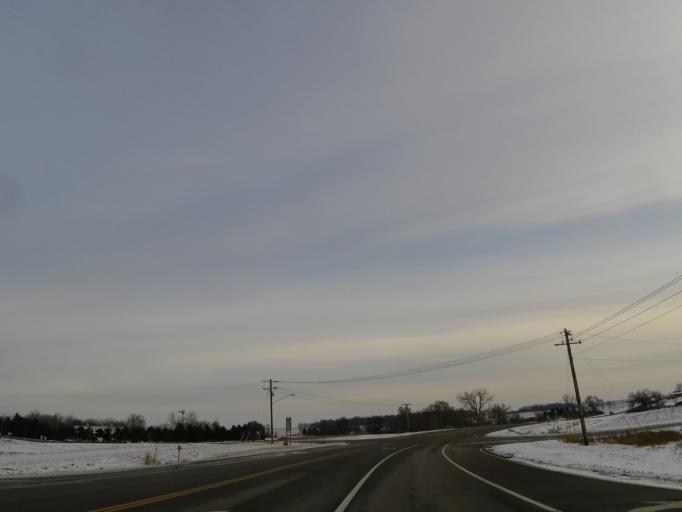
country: US
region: Minnesota
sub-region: Carver County
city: Carver
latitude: 44.7919
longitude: -93.6430
